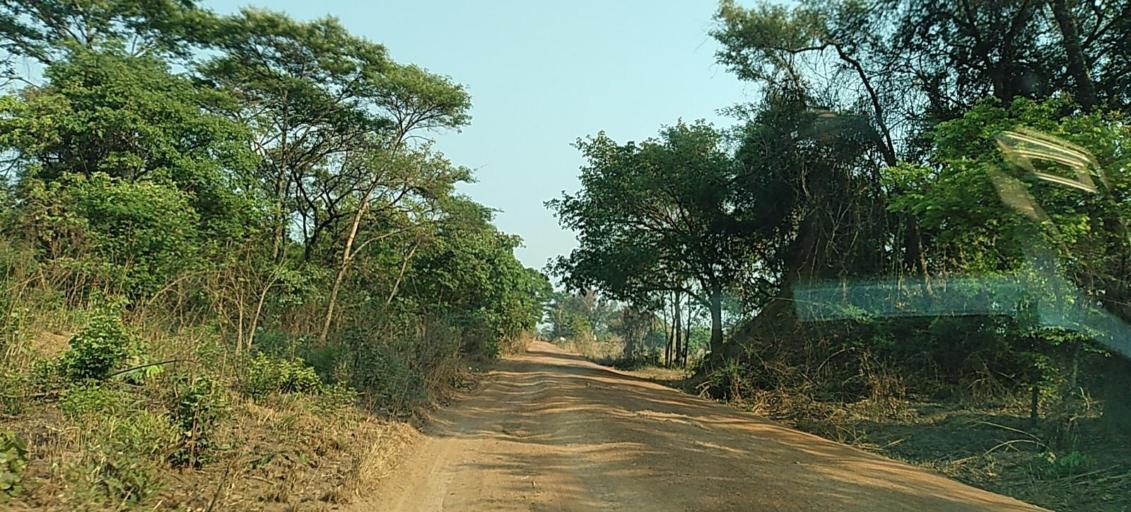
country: ZM
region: Copperbelt
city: Chingola
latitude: -12.8395
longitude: 27.5448
